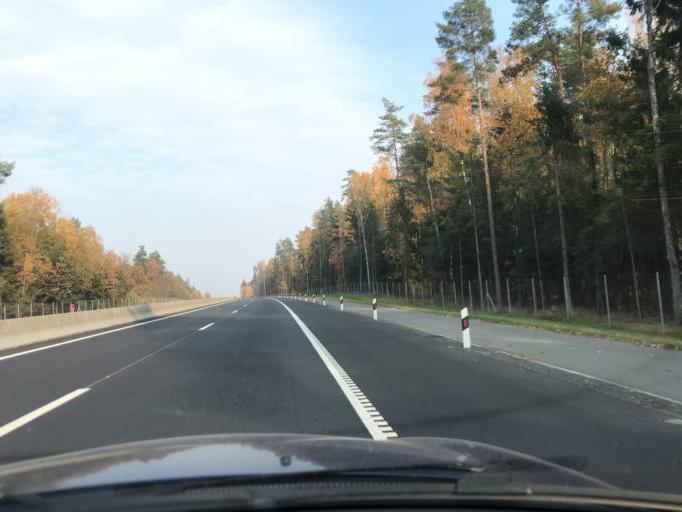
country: BY
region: Grodnenskaya
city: Shchuchin
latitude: 53.6689
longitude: 24.8273
